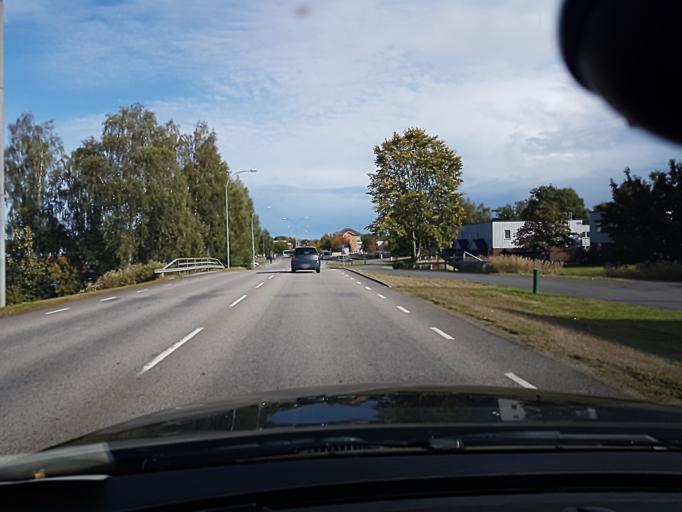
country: SE
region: Kronoberg
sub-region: Vaxjo Kommun
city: Vaexjoe
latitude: 56.8543
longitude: 14.8184
